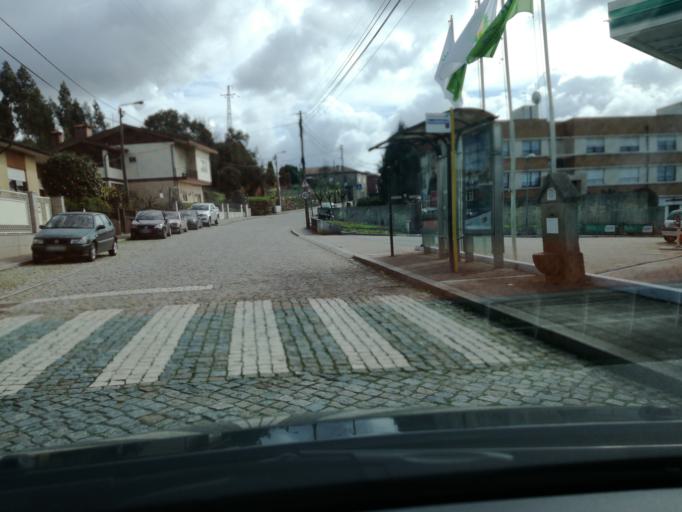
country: PT
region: Porto
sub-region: Valongo
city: Alfena
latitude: 41.2556
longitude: -8.5458
